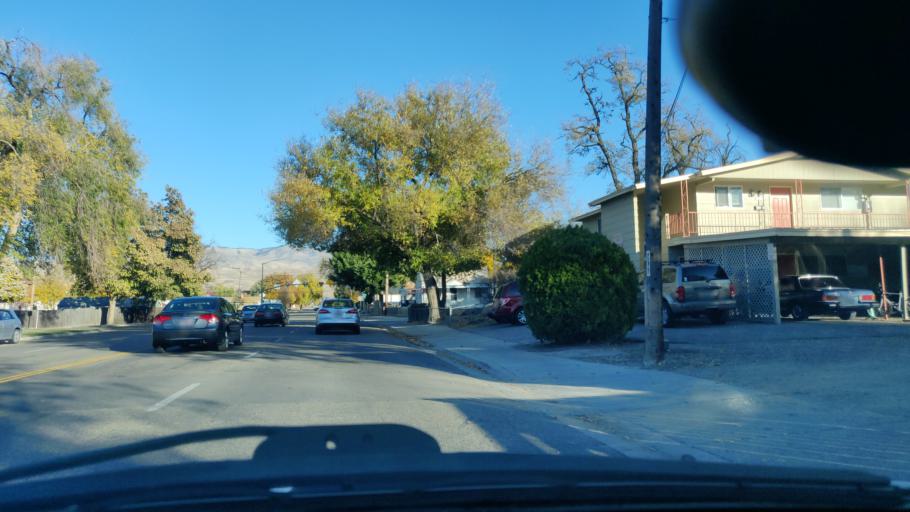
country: US
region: Idaho
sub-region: Ada County
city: Boise
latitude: 43.5984
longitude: -116.2006
